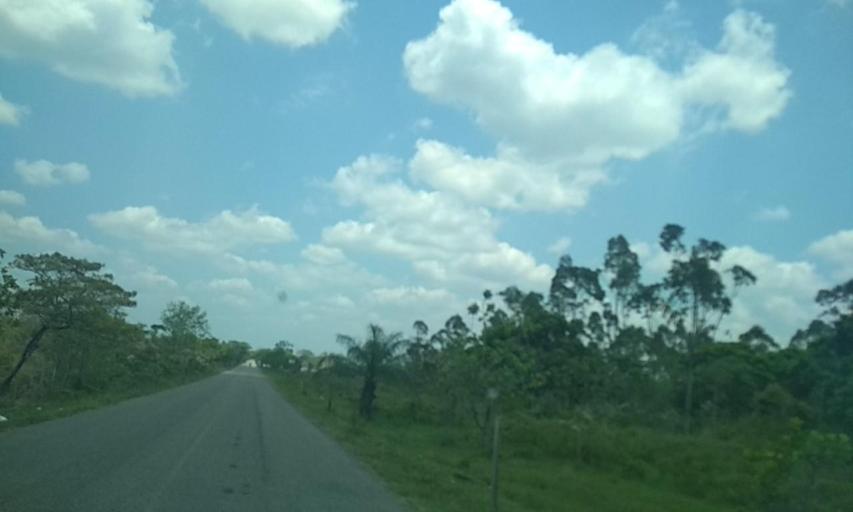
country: MX
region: Tabasco
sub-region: Huimanguillo
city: Francisco Rueda
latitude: 17.7741
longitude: -93.8156
